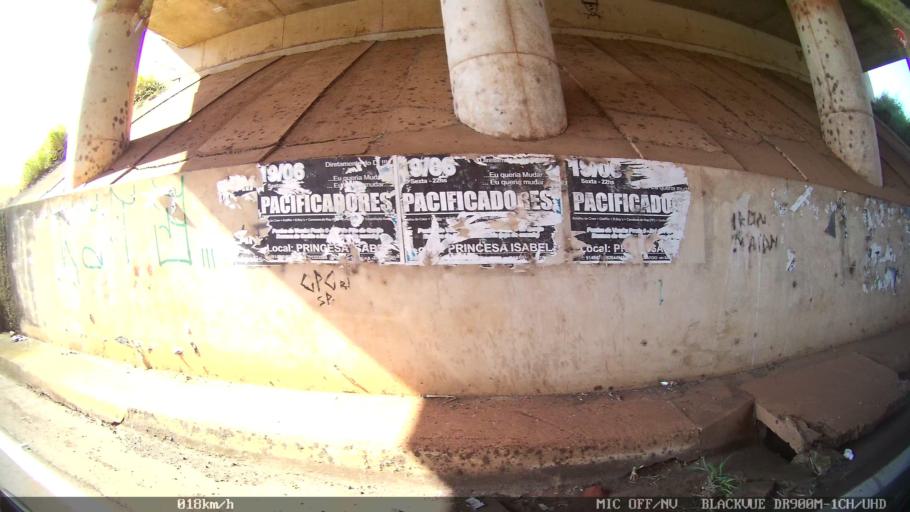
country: BR
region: Sao Paulo
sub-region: Batatais
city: Batatais
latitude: -20.9159
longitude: -47.5838
